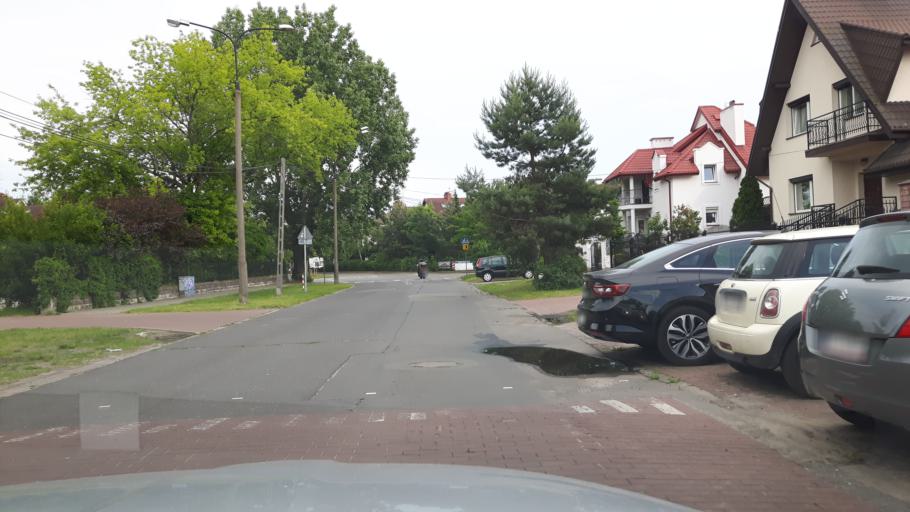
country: PL
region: Masovian Voivodeship
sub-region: Warszawa
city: Rembertow
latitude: 52.2355
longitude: 21.1332
